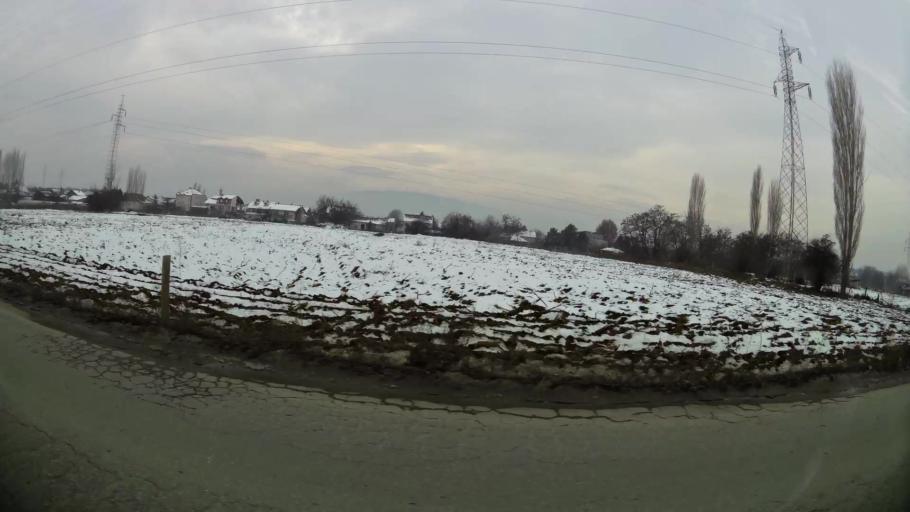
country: MK
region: Butel
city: Butel
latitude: 42.0407
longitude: 21.4526
